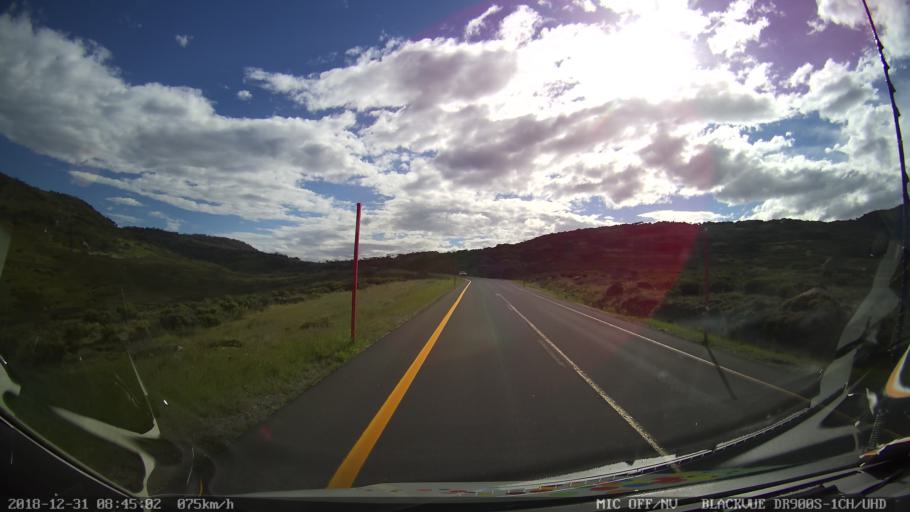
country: AU
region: New South Wales
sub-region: Snowy River
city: Jindabyne
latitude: -36.3791
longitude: 148.4607
